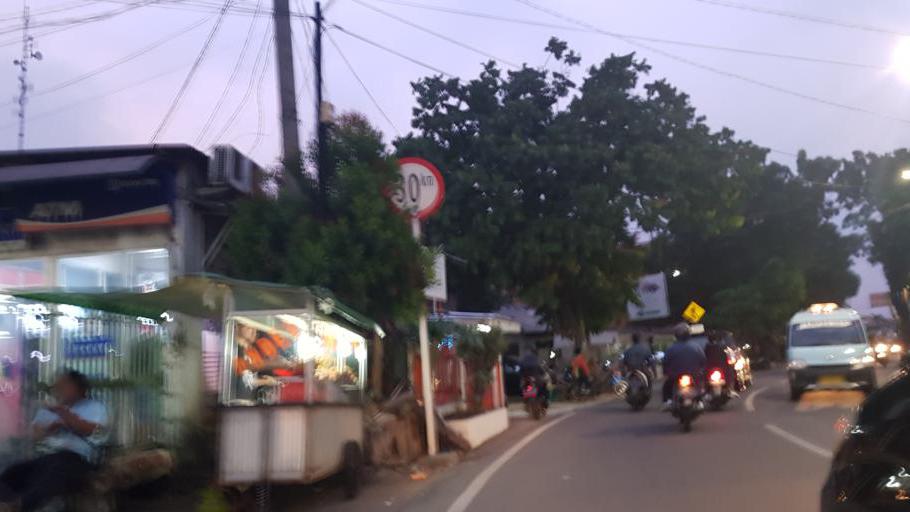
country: ID
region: West Java
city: Depok
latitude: -6.3630
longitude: 106.8022
